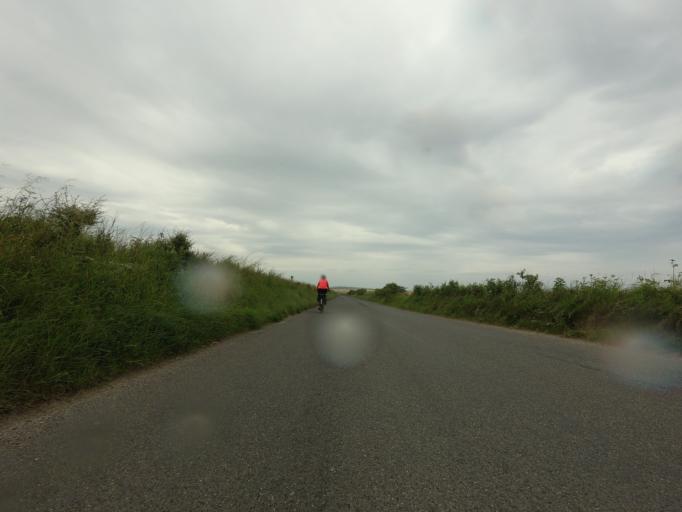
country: GB
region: Scotland
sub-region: Aberdeenshire
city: Whitehills
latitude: 57.6728
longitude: -2.6345
